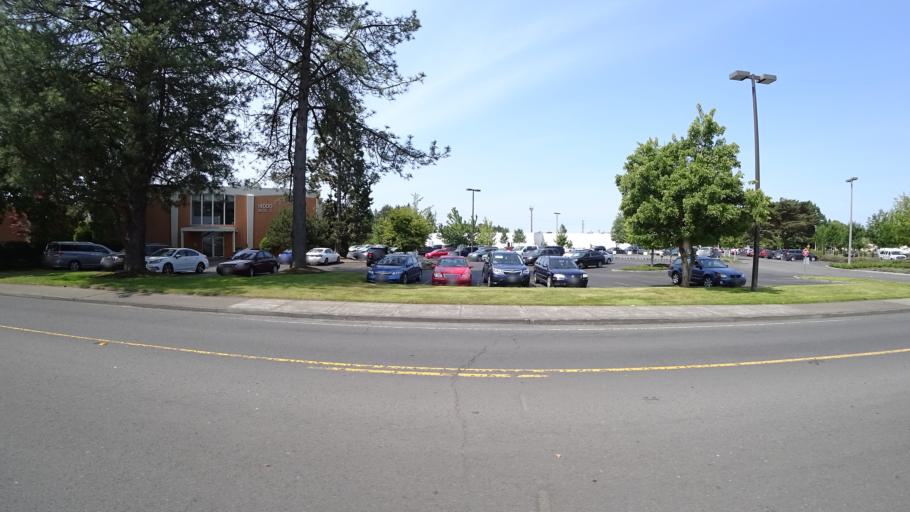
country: US
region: Oregon
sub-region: Washington County
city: Cedar Mill
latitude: 45.5265
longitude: -122.8218
